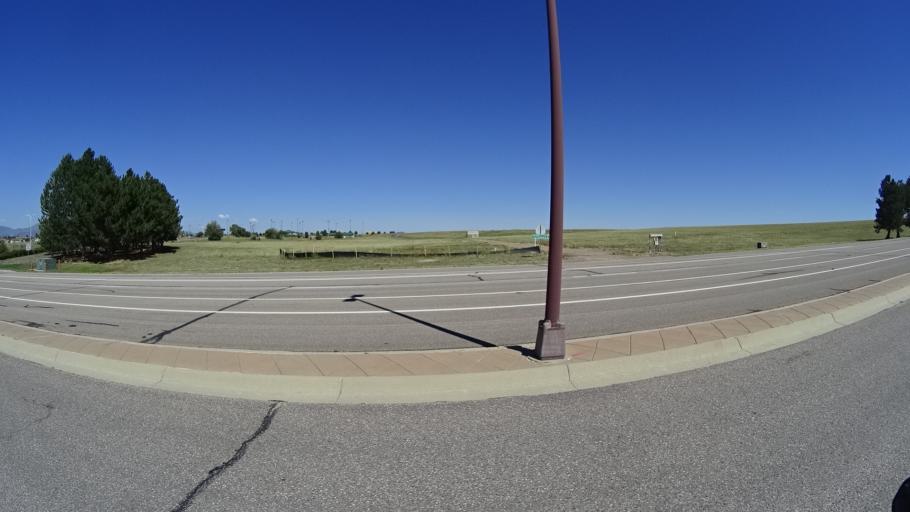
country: US
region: Colorado
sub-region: El Paso County
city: Security-Widefield
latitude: 38.7811
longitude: -104.7195
